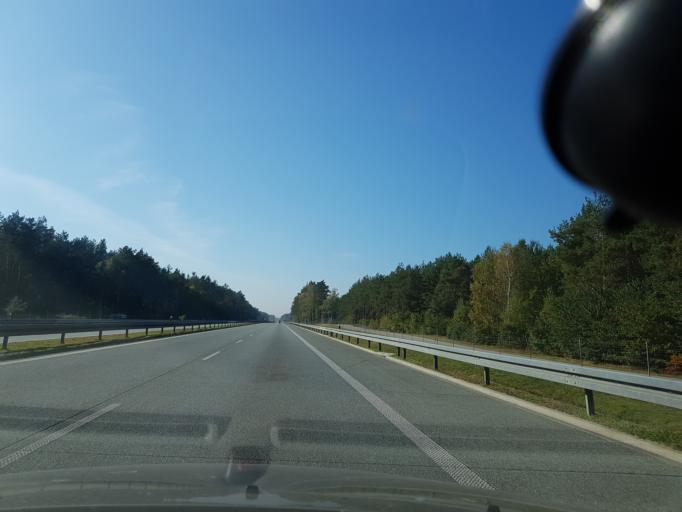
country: PL
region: Lodz Voivodeship
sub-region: Powiat tomaszowski
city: Czerniewice
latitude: 51.6402
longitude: 20.1253
